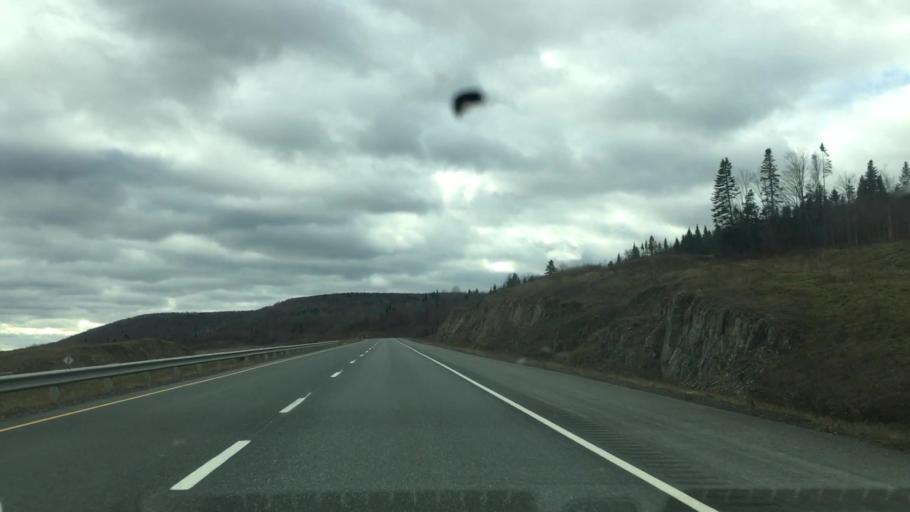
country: US
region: Maine
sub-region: Aroostook County
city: Fort Fairfield
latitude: 46.7031
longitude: -67.7393
